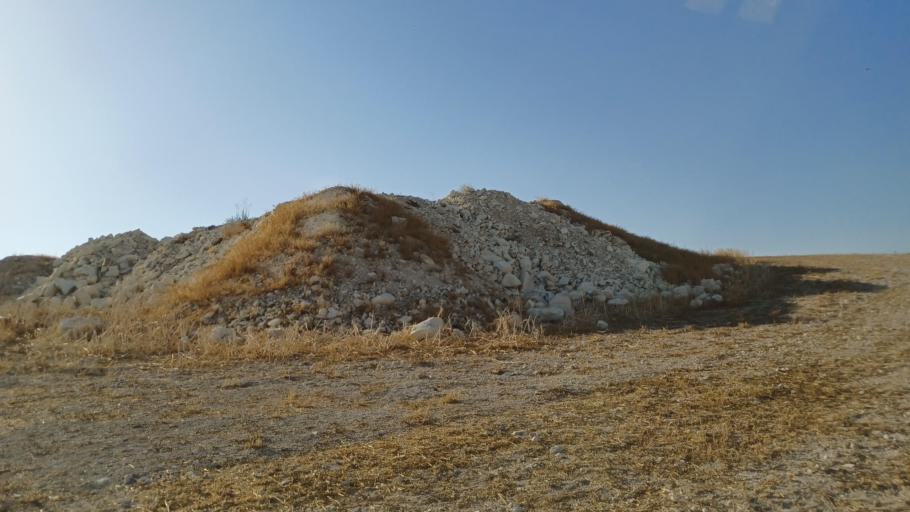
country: CY
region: Larnaka
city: Athienou
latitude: 35.0348
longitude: 33.5290
